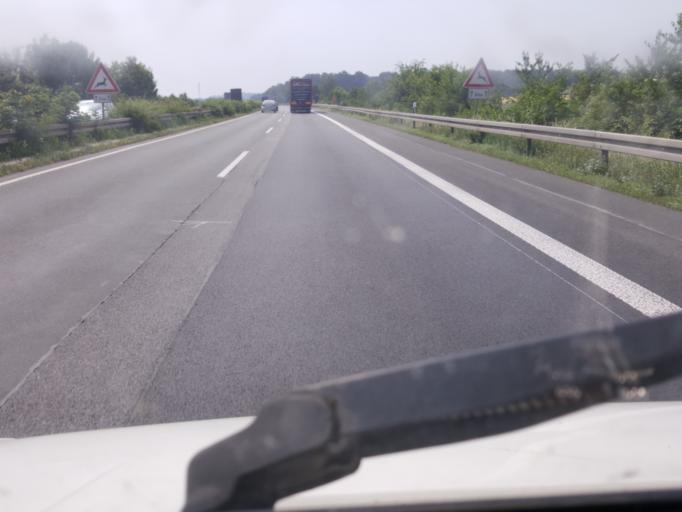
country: DE
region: North Rhine-Westphalia
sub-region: Regierungsbezirk Detmold
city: Paderborn
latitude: 51.6385
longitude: 8.7195
